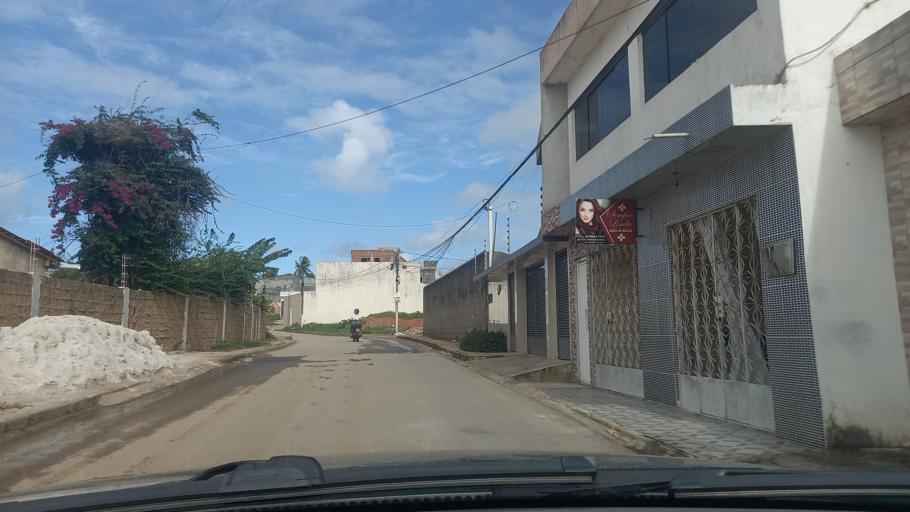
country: BR
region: Pernambuco
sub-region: Vitoria De Santo Antao
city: Vitoria de Santo Antao
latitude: -8.1072
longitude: -35.3050
